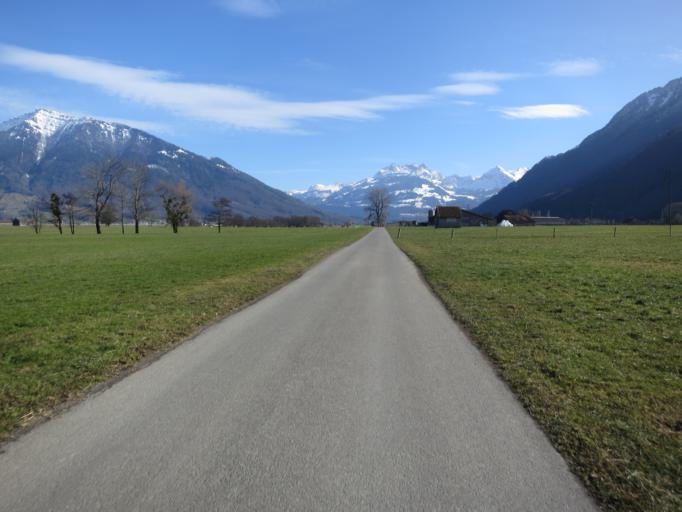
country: CH
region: Schwyz
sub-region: Bezirk March
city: Reichenburg
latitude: 47.1701
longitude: 8.9961
